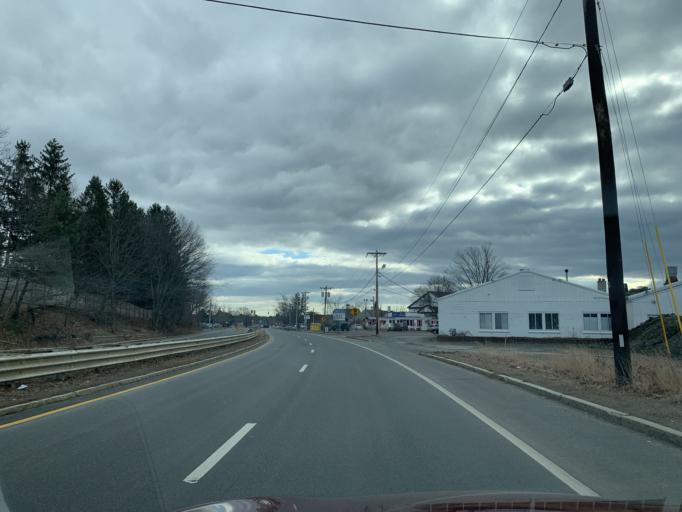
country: US
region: Massachusetts
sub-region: Essex County
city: Newburyport
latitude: 42.8020
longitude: -70.8788
